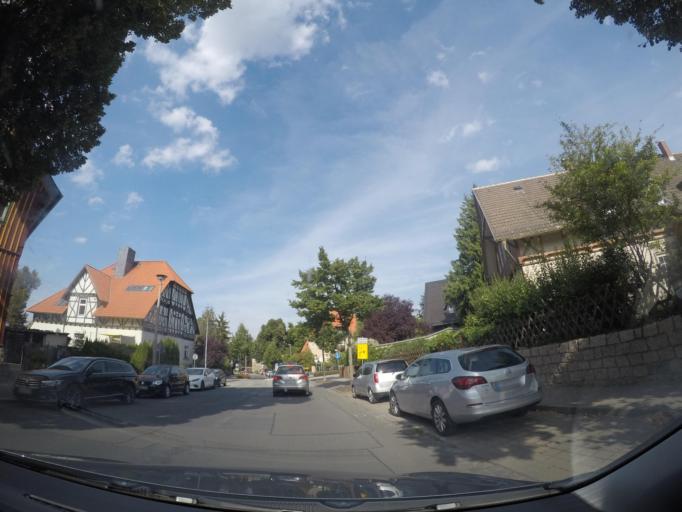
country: DE
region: Saxony-Anhalt
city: Wernigerode
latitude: 51.8299
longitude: 10.7802
